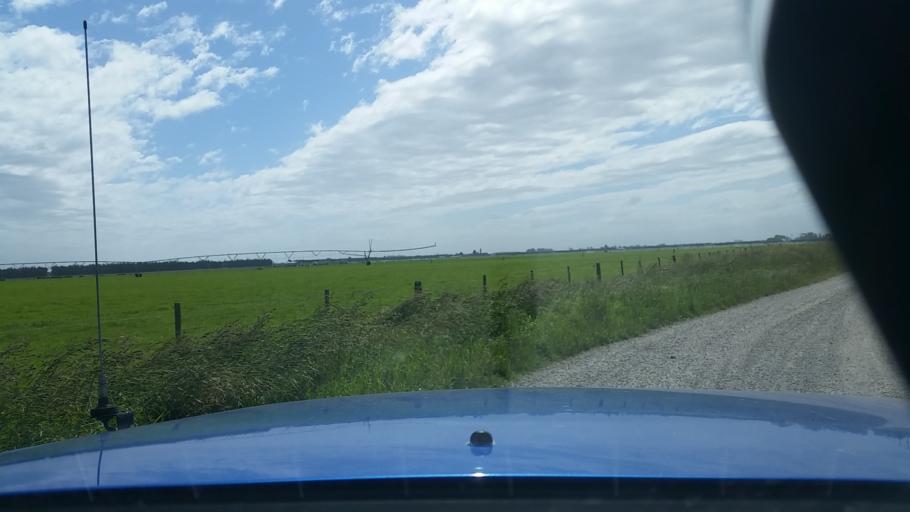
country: NZ
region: Canterbury
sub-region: Ashburton District
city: Rakaia
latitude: -43.9771
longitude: 171.9686
